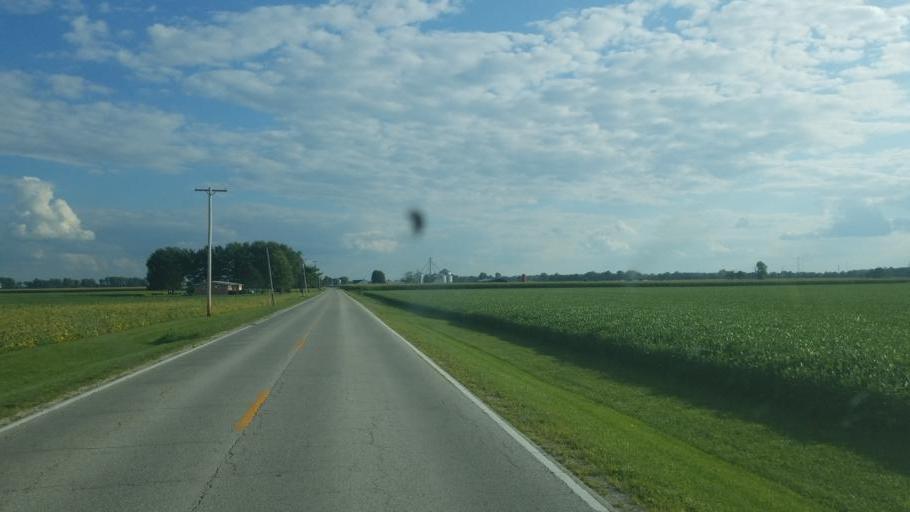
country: US
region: Ohio
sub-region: Sandusky County
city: Ballville
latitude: 41.2622
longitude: -83.1313
